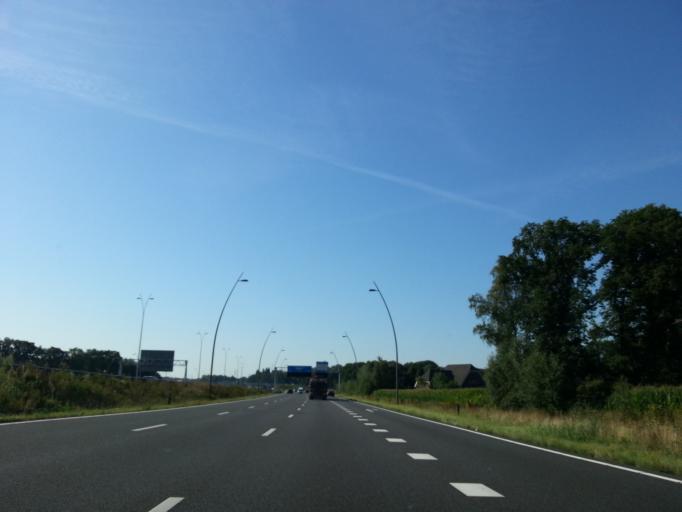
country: NL
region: North Brabant
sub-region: Gemeente Eindhoven
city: Meerhoven
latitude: 51.4655
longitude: 5.4054
